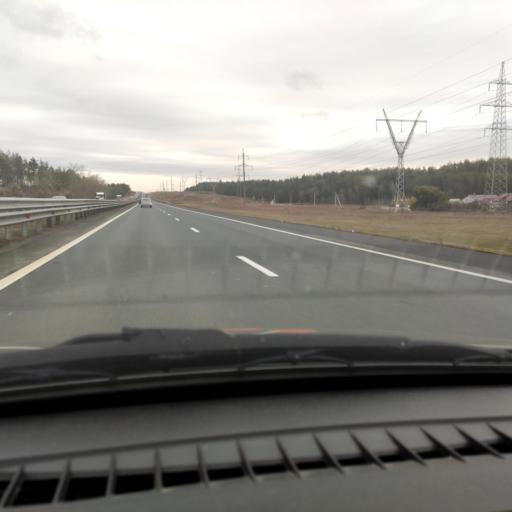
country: RU
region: Samara
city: Povolzhskiy
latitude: 53.5142
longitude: 49.6270
